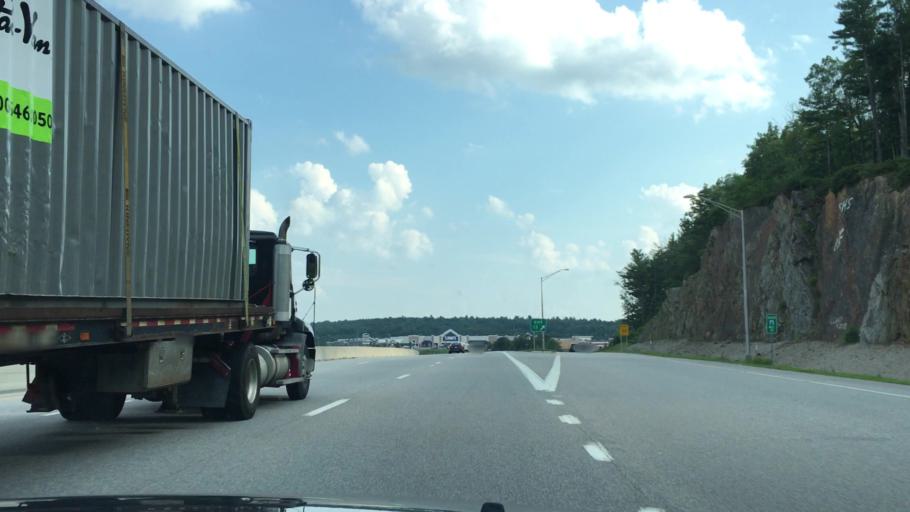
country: US
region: New Hampshire
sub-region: Strafford County
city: Rochester
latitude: 43.2999
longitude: -70.9946
